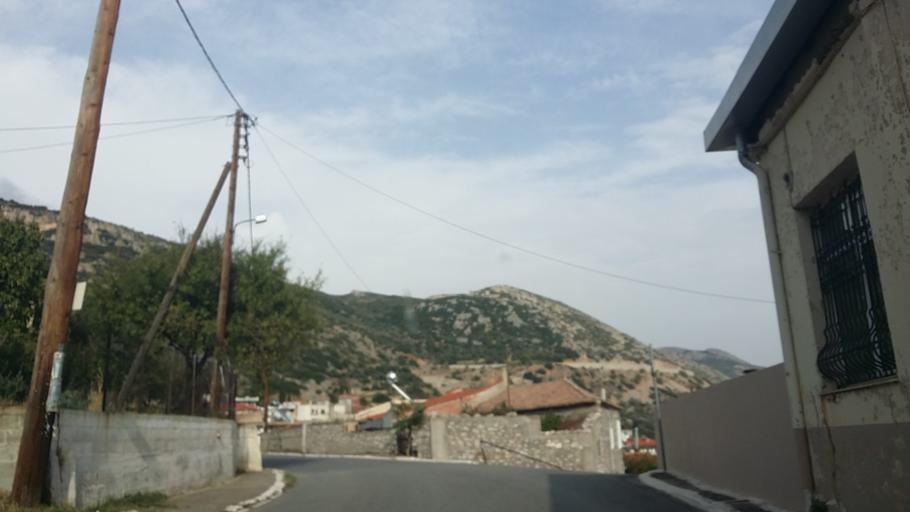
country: GR
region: Central Greece
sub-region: Nomos Voiotias
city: Korini
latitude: 38.2582
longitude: 22.9091
